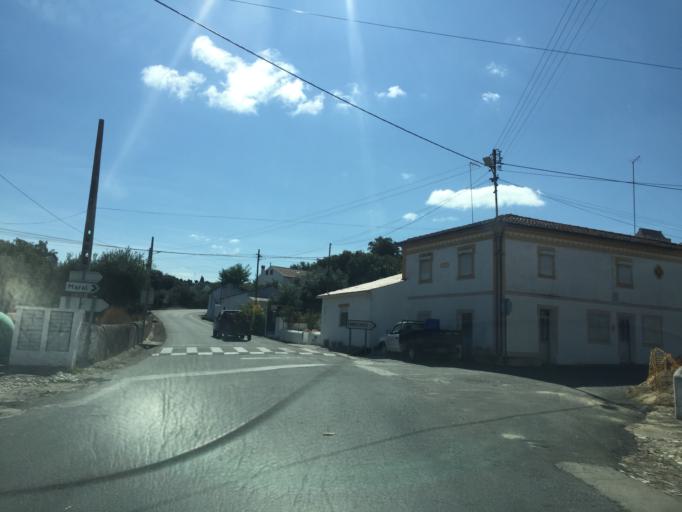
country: PT
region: Portalegre
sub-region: Marvao
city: Marvao
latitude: 39.4247
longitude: -7.3532
